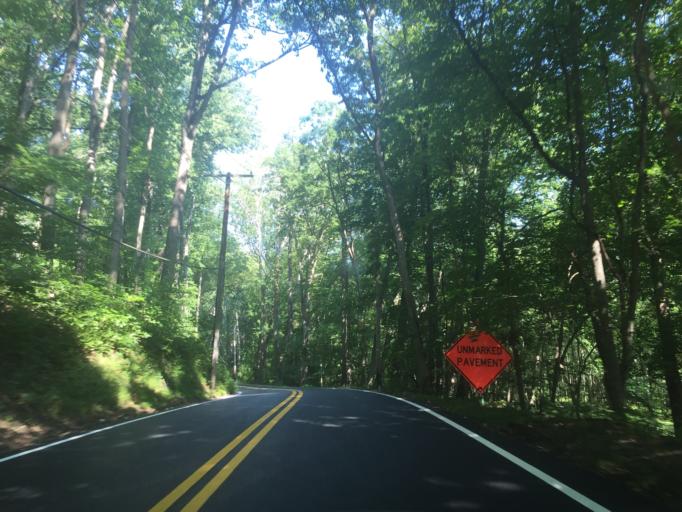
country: US
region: Maryland
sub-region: Baltimore County
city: Mays Chapel
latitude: 39.4118
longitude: -76.6686
